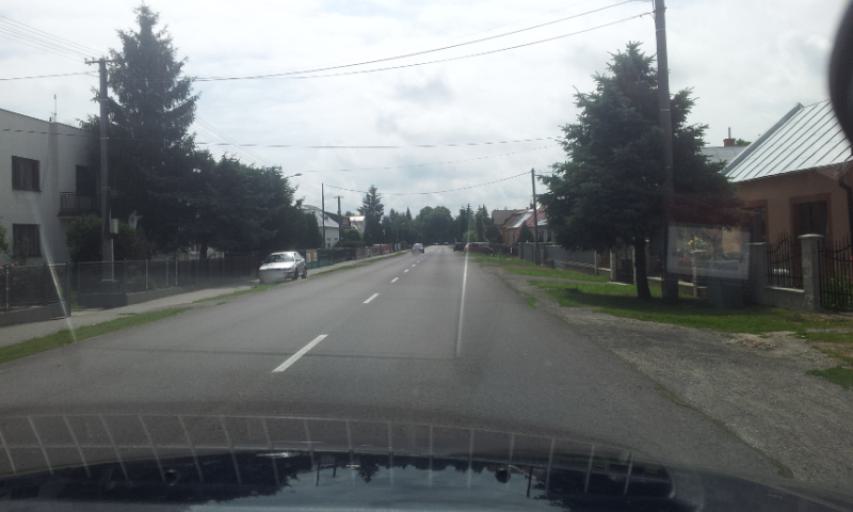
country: SK
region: Kosicky
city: Michalovce
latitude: 48.7376
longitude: 21.9487
